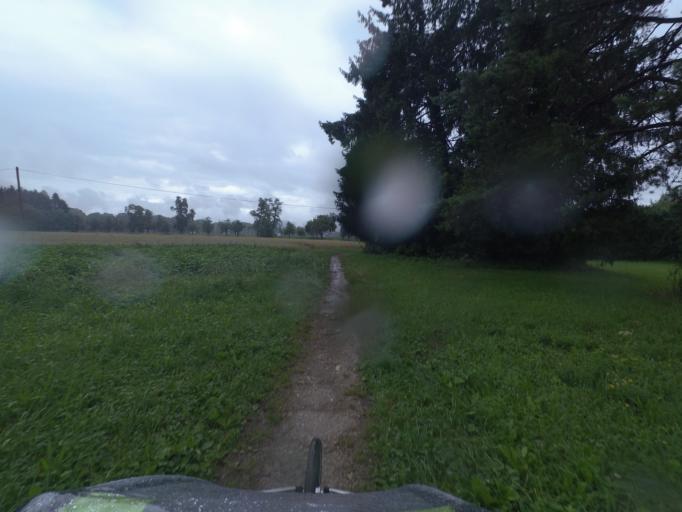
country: AT
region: Salzburg
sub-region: Politischer Bezirk Salzburg-Umgebung
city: Anif
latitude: 47.7661
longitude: 13.0560
